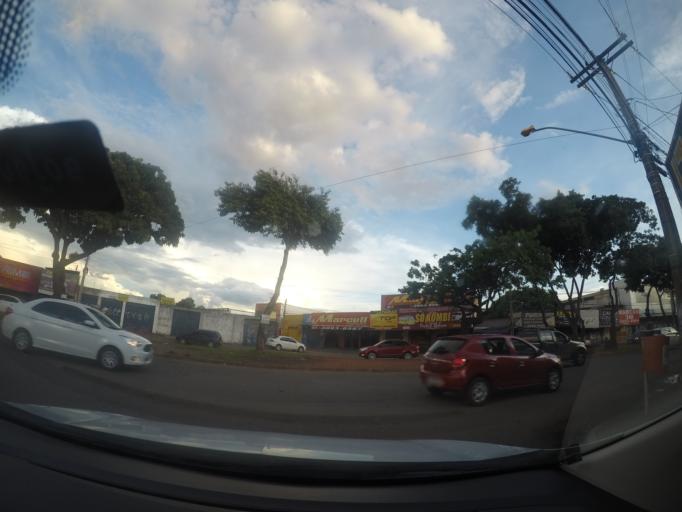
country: BR
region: Goias
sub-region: Goiania
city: Goiania
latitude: -16.6913
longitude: -49.3162
